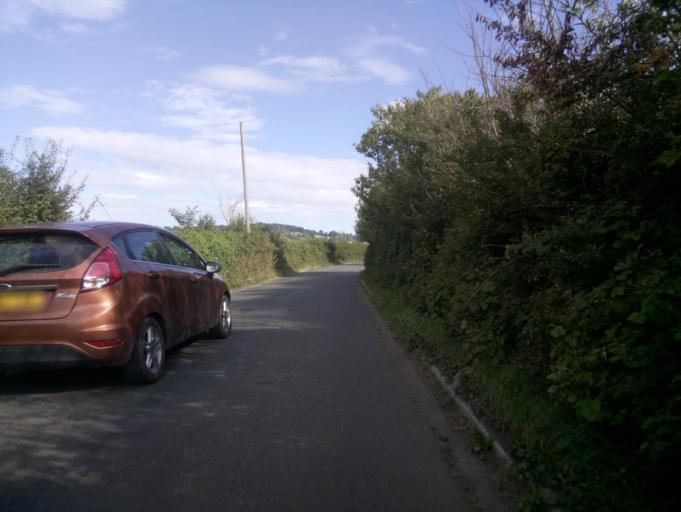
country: GB
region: England
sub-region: Gloucestershire
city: Gloucester
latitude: 51.8097
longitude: -2.2550
